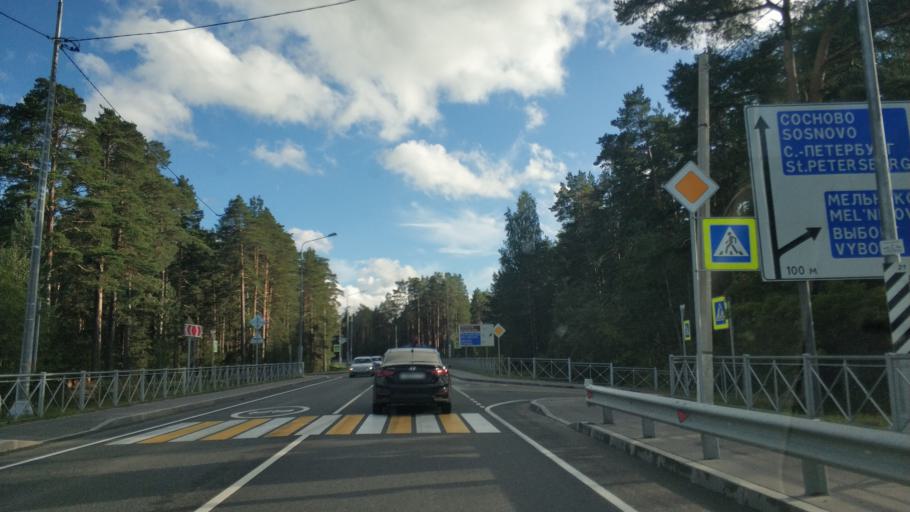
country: RU
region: Leningrad
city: Priozersk
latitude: 60.9984
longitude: 30.1825
